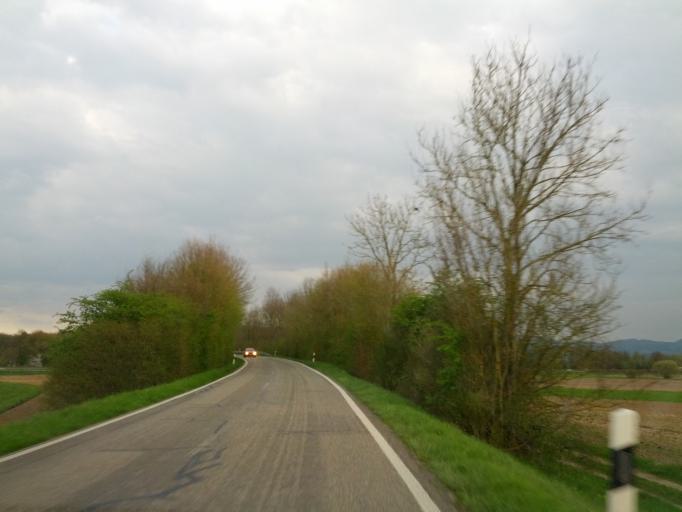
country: DE
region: Baden-Wuerttemberg
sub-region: Freiburg Region
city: Teningen
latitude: 48.0891
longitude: 7.7939
